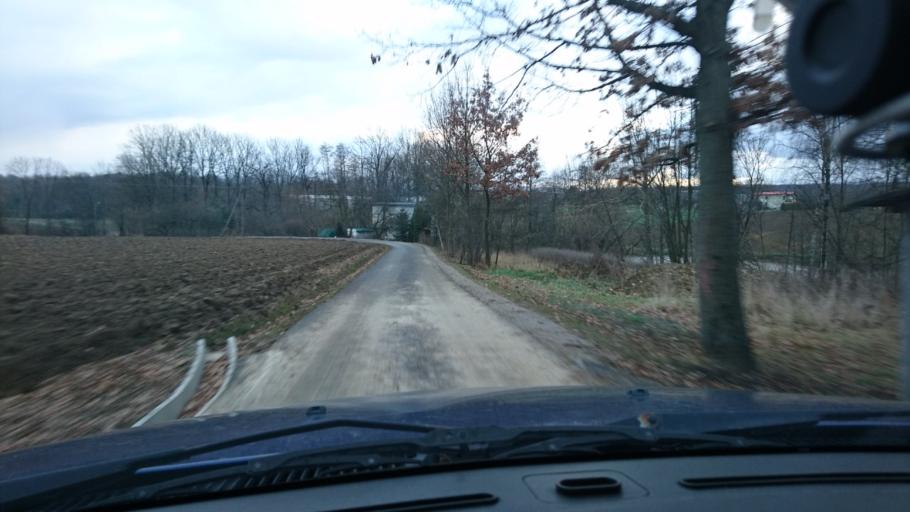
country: PL
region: Silesian Voivodeship
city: Janowice
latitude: 49.8956
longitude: 19.0792
